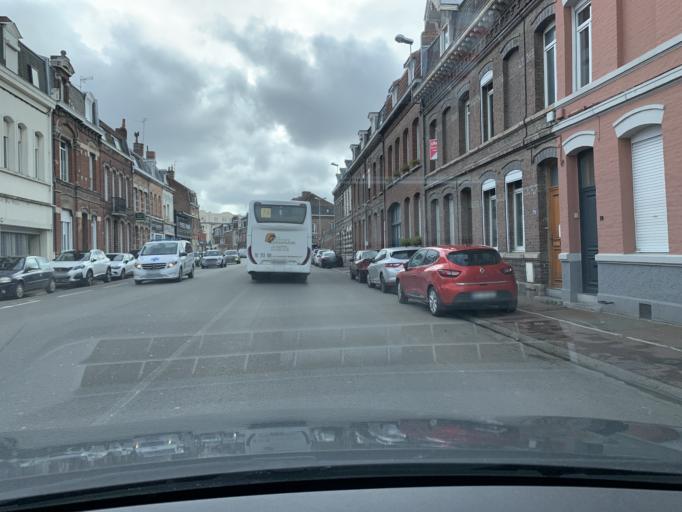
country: FR
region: Nord-Pas-de-Calais
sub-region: Departement du Nord
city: Douai
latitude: 50.3626
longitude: 3.0784
